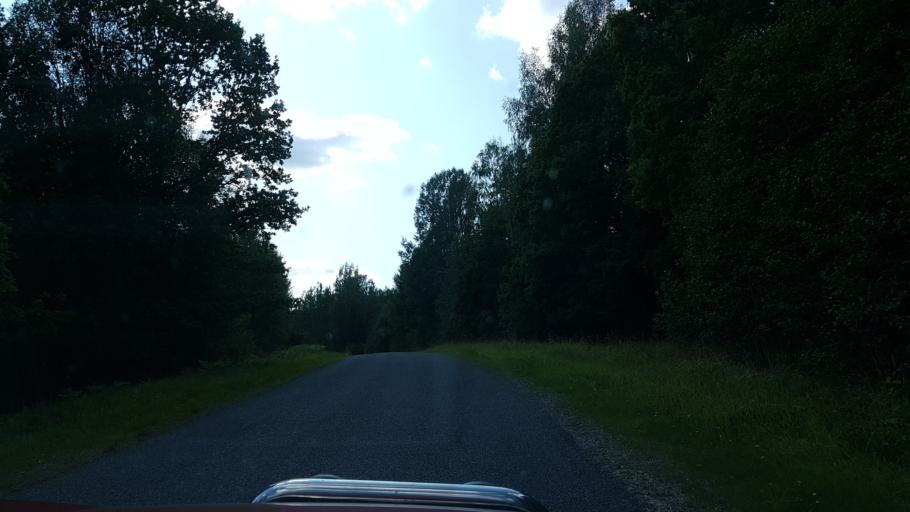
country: LV
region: Aluksnes Rajons
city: Aluksne
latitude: 57.6006
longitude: 27.0929
